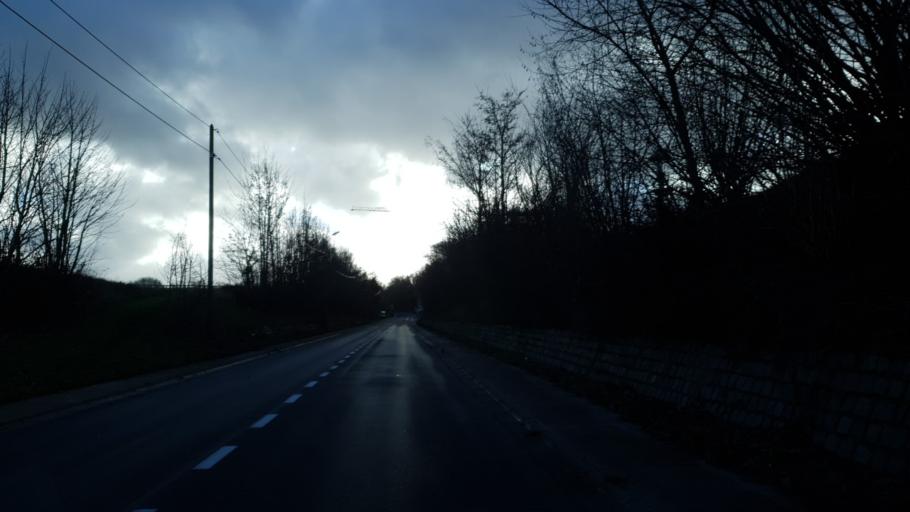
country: BE
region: Flanders
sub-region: Provincie Vlaams-Brabant
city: Kortenberg
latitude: 50.8719
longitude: 4.5791
